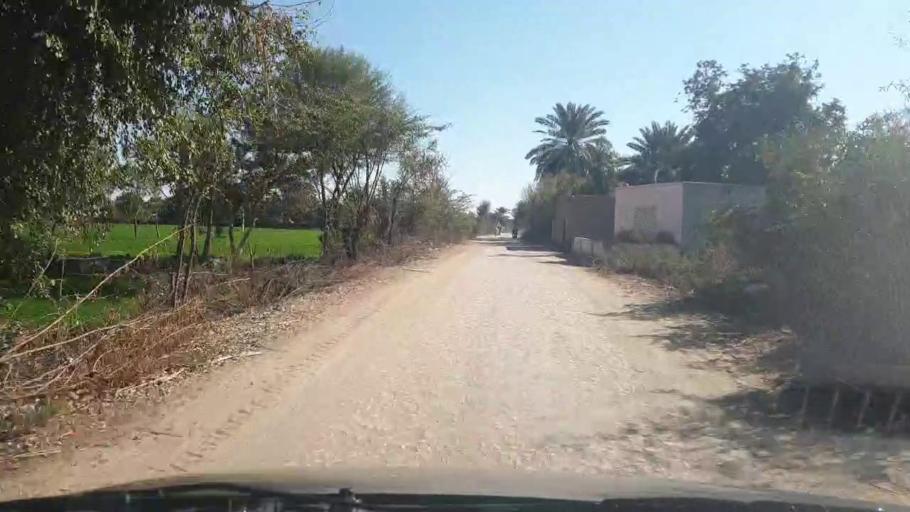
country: PK
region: Sindh
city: Bozdar
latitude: 27.0648
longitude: 68.6205
